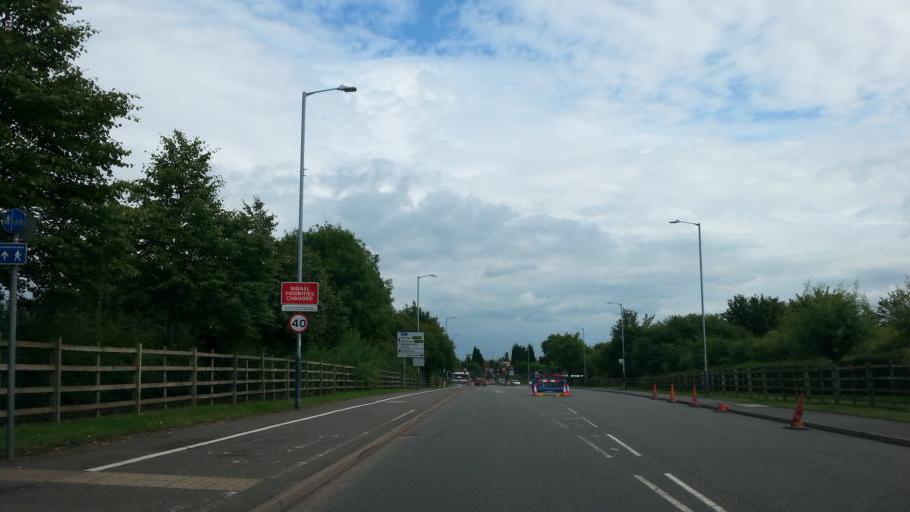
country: GB
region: England
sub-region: Coventry
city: Keresley
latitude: 52.4525
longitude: -1.5125
